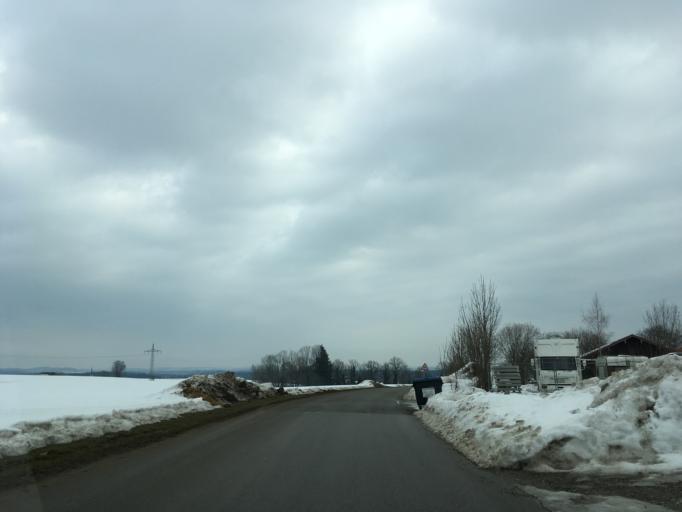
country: DE
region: Bavaria
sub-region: Upper Bavaria
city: Bad Endorf
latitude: 47.9108
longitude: 12.3253
